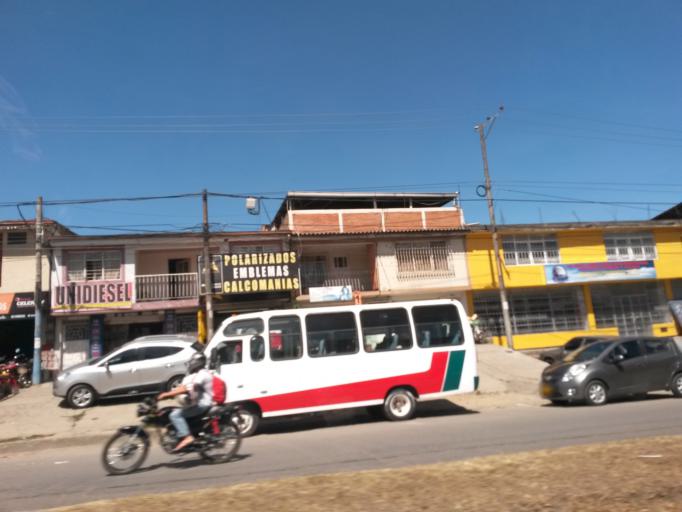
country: CO
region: Cauca
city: Popayan
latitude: 2.4489
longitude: -76.6236
